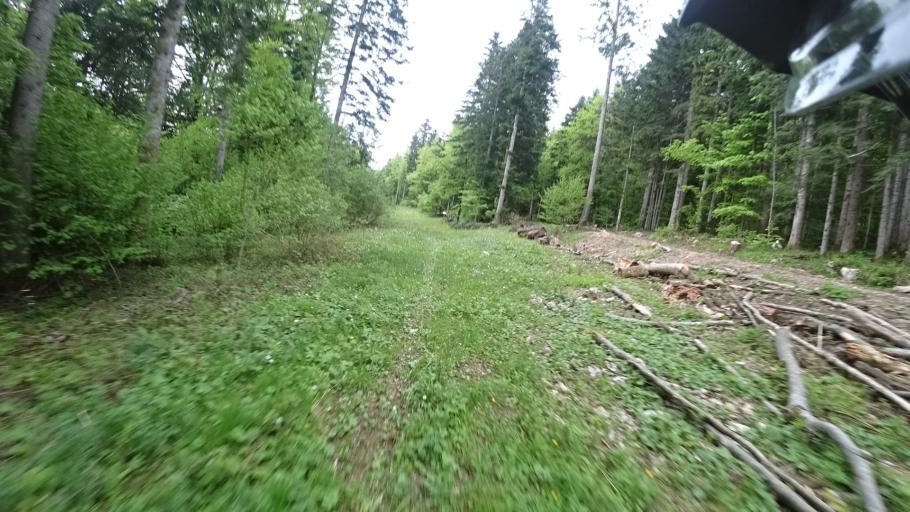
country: HR
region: Karlovacka
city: Plaski
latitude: 44.9659
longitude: 15.4032
